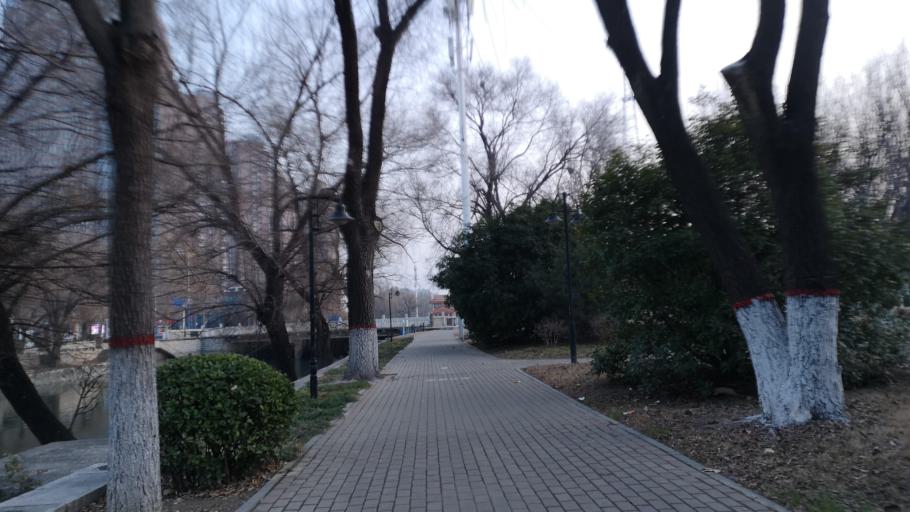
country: CN
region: Henan Sheng
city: Zhongyuanlu
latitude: 35.7765
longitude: 115.0780
